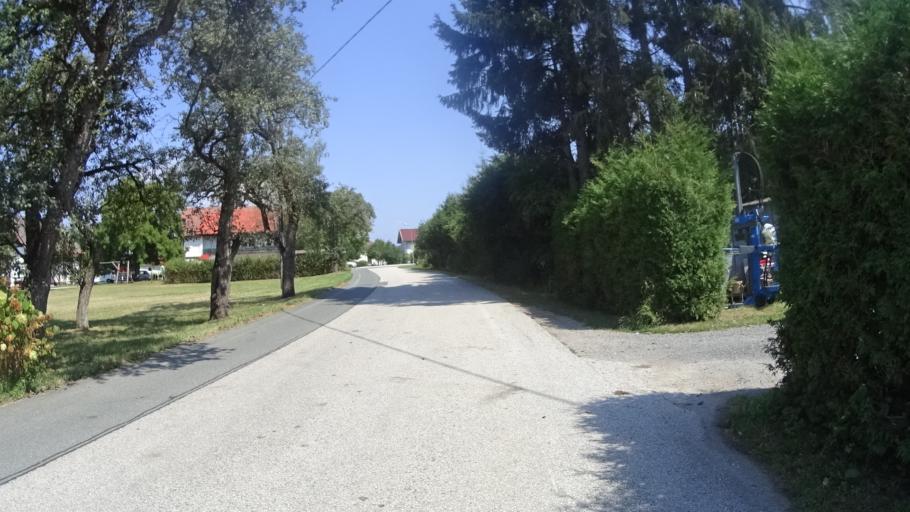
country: AT
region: Carinthia
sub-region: Politischer Bezirk Volkermarkt
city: Eberndorf
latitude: 46.5733
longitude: 14.6331
